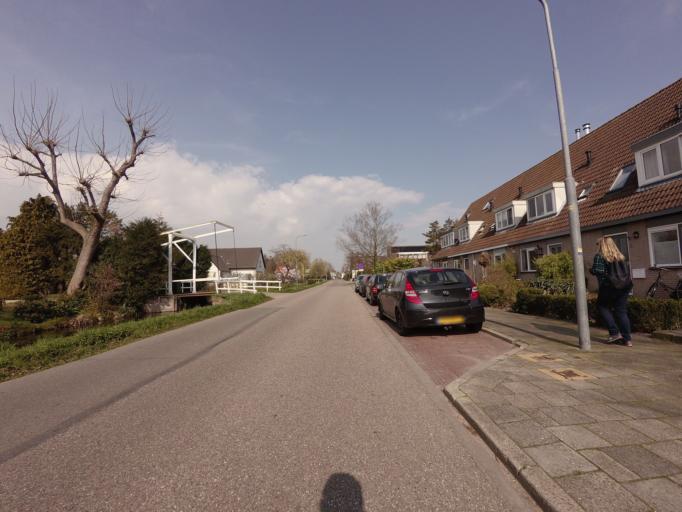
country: NL
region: North Holland
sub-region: Gemeente Wijdemeren
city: Kortenhoef
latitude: 52.2612
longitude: 5.0960
